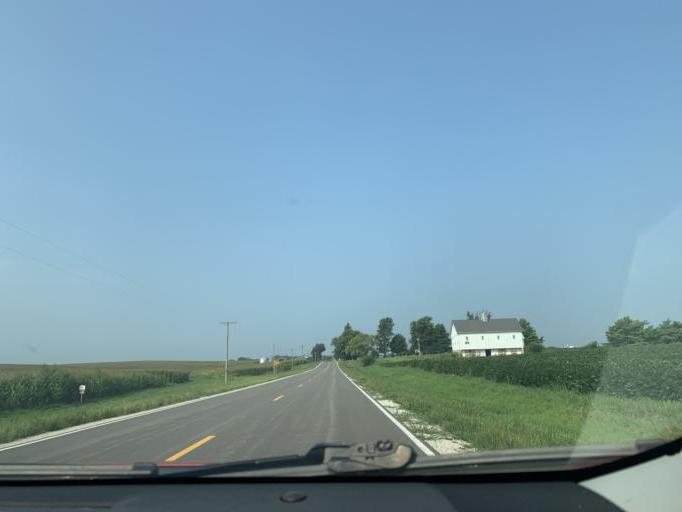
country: US
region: Illinois
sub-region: Whiteside County
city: Sterling
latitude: 41.8442
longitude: -89.7486
